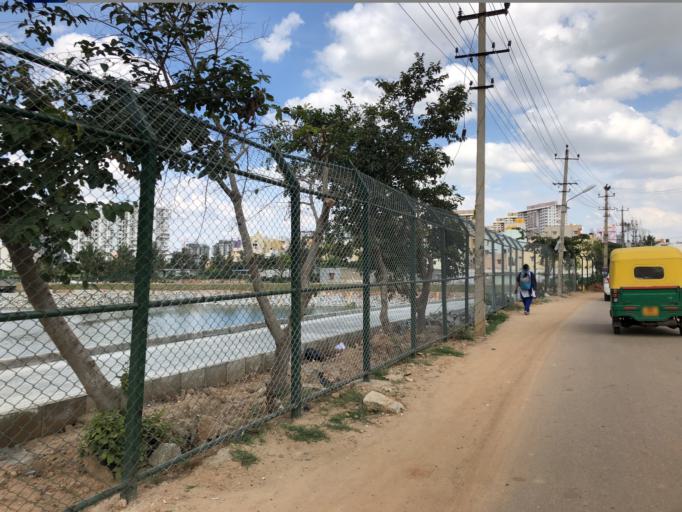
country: IN
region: Karnataka
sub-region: Bangalore Urban
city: Bangalore
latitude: 12.9904
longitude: 77.6953
